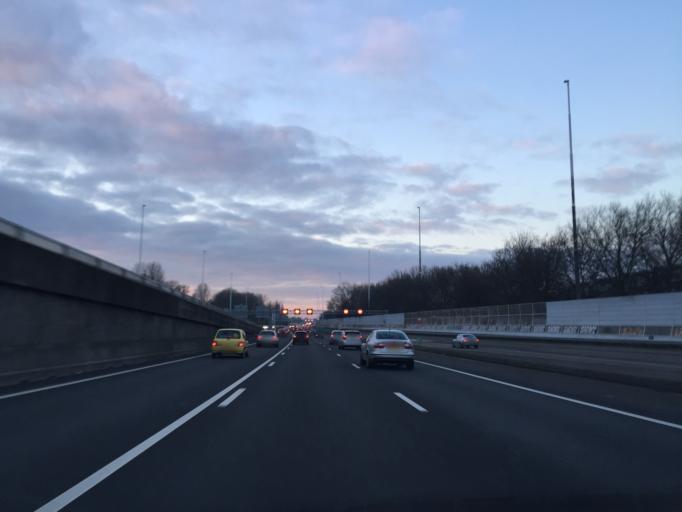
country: NL
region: South Holland
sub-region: Gemeente Rotterdam
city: Delfshaven
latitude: 51.9336
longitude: 4.4362
